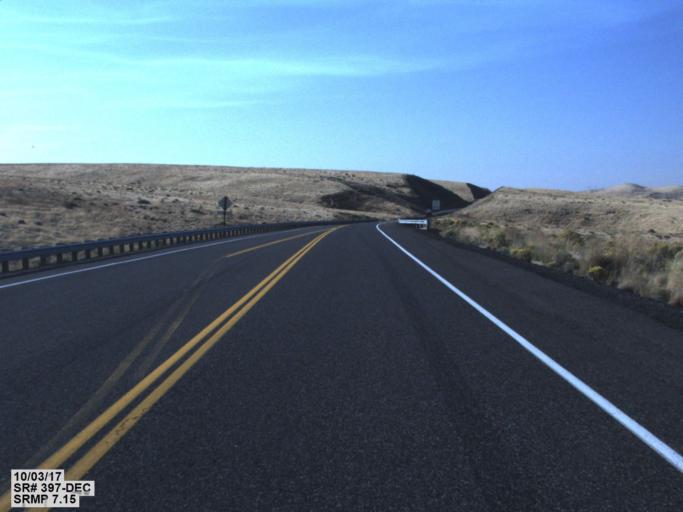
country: US
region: Washington
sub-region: Benton County
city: Finley
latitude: 46.1272
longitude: -119.0684
